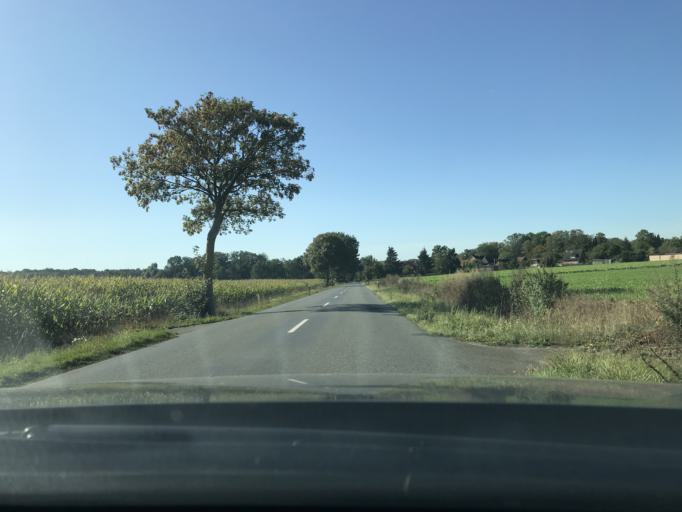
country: DE
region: Lower Saxony
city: Gerdau
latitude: 52.9703
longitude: 10.4248
